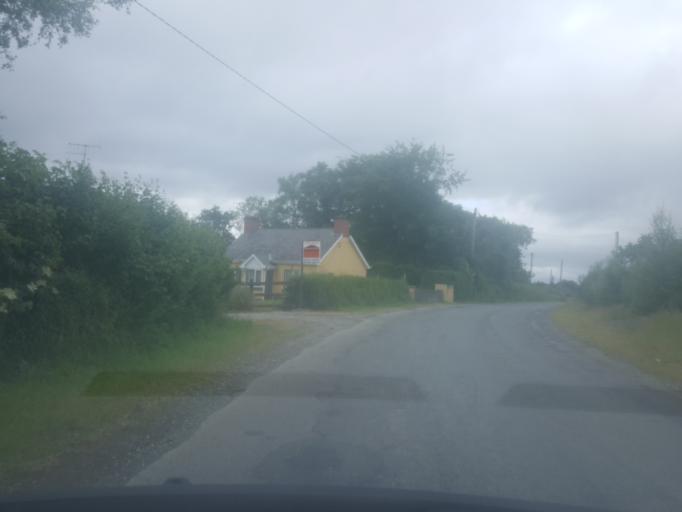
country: IE
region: Munster
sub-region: Ciarrai
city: Cill Airne
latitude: 52.0823
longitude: -9.4940
